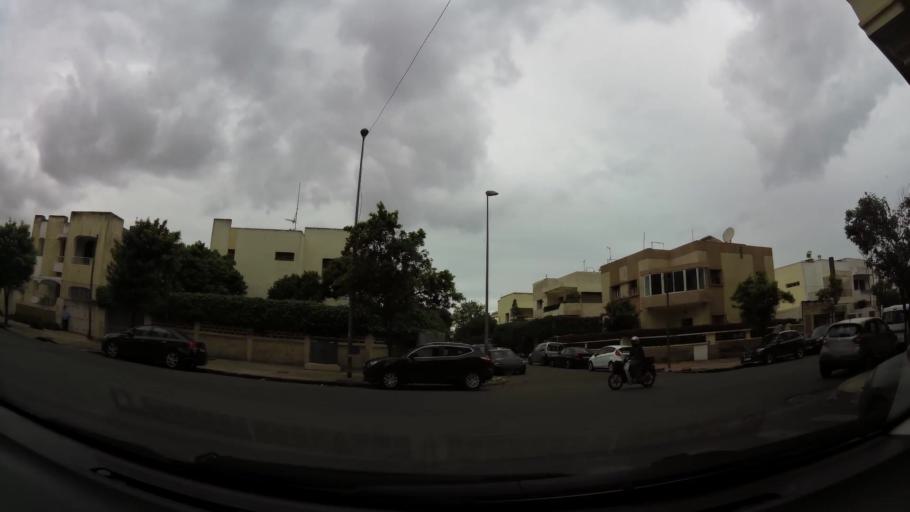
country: MA
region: Grand Casablanca
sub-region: Casablanca
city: Casablanca
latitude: 33.5931
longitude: -7.6450
